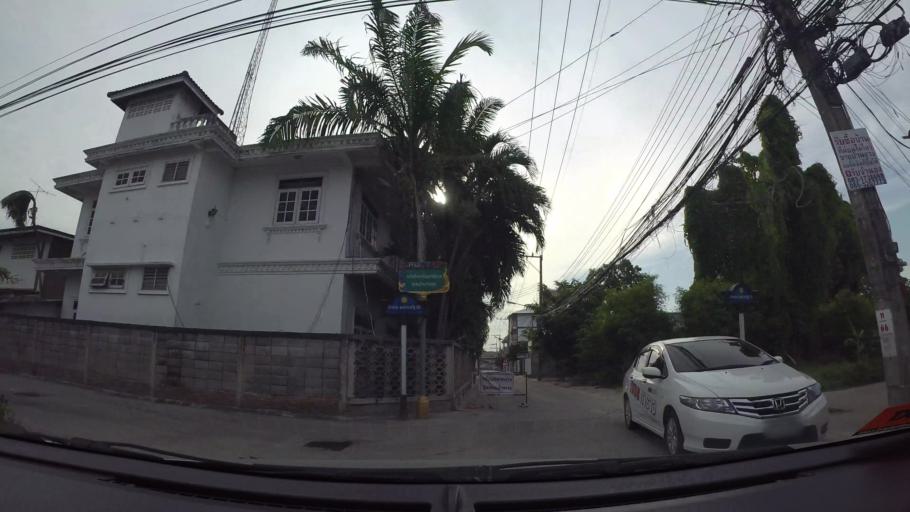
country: TH
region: Chon Buri
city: Chon Buri
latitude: 13.3355
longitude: 100.9679
